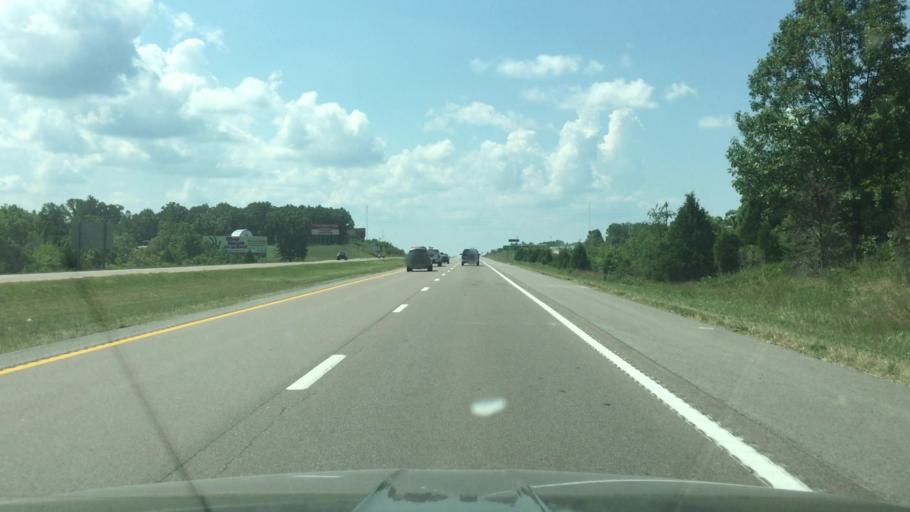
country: US
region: Missouri
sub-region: Miller County
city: Eldon
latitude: 38.2986
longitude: -92.5801
